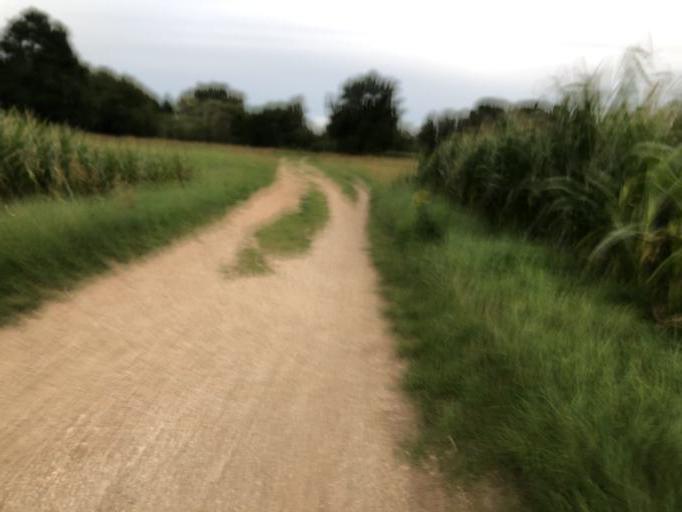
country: DE
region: Bavaria
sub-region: Regierungsbezirk Mittelfranken
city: Erlangen
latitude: 49.6003
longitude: 10.9930
